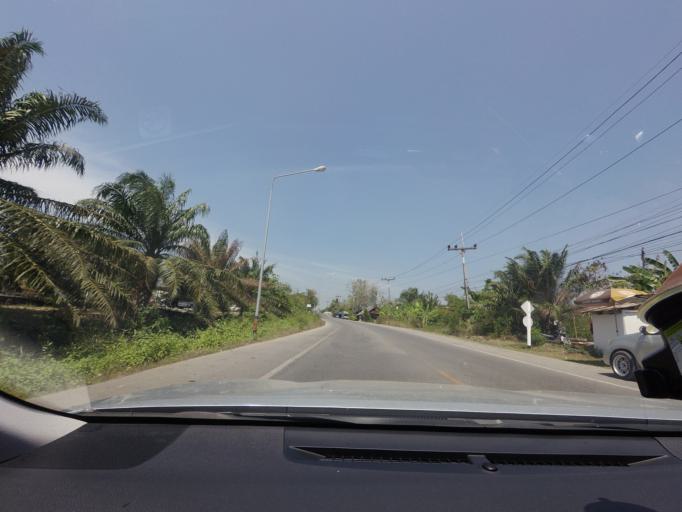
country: TH
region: Surat Thani
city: Tha Chang
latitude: 9.2019
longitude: 99.2447
